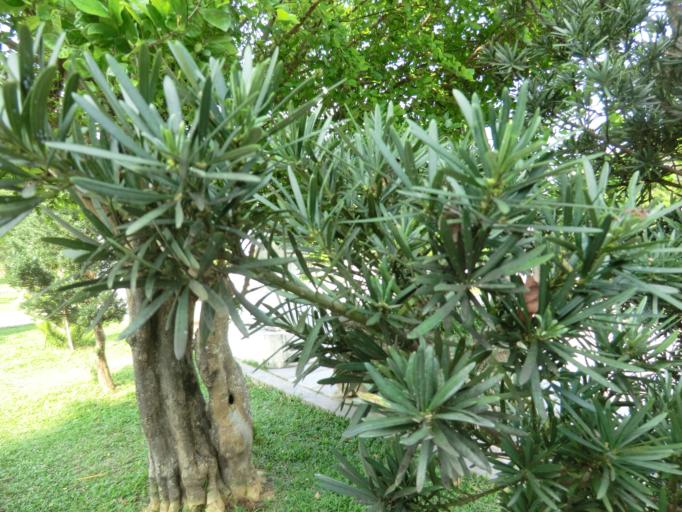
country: VN
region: Da Nang
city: Son Tra
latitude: 16.0998
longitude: 108.2774
